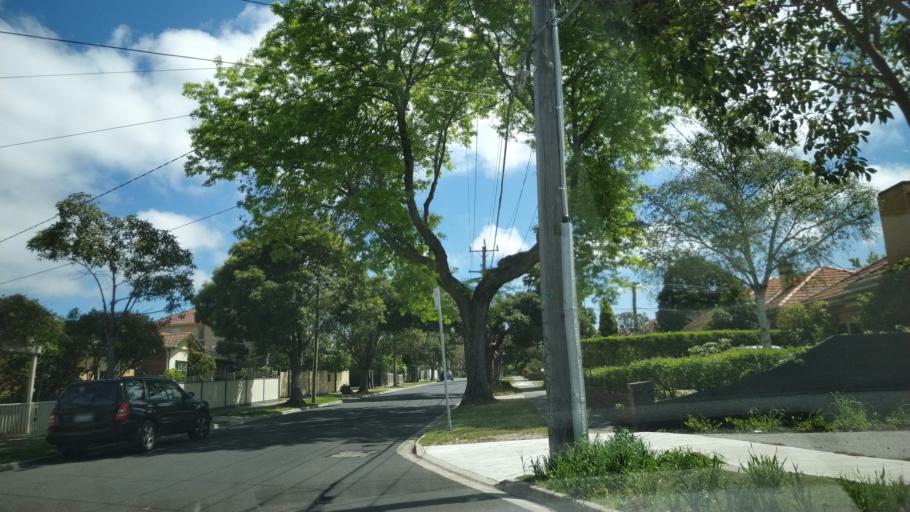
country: AU
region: Victoria
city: Murrumbeena
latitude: -37.9026
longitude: 145.0683
